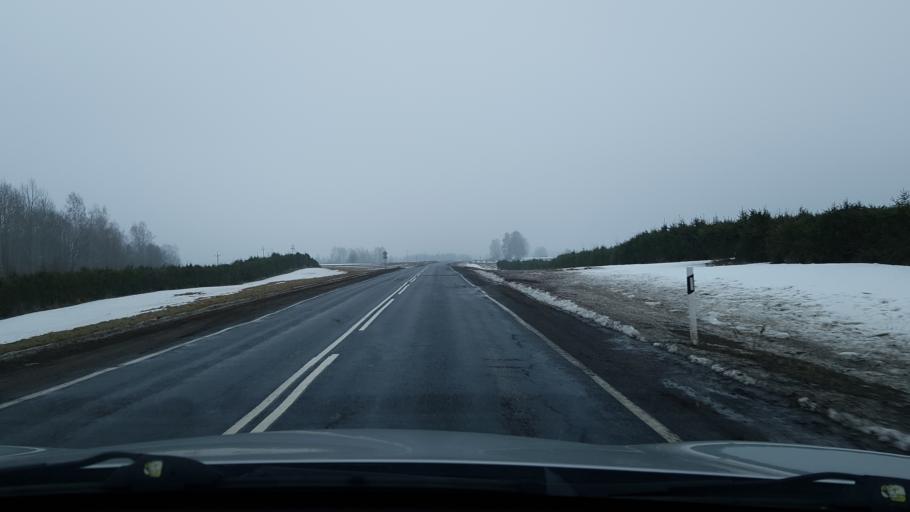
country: EE
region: Viljandimaa
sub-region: Viiratsi vald
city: Viiratsi
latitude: 58.2600
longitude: 25.7100
